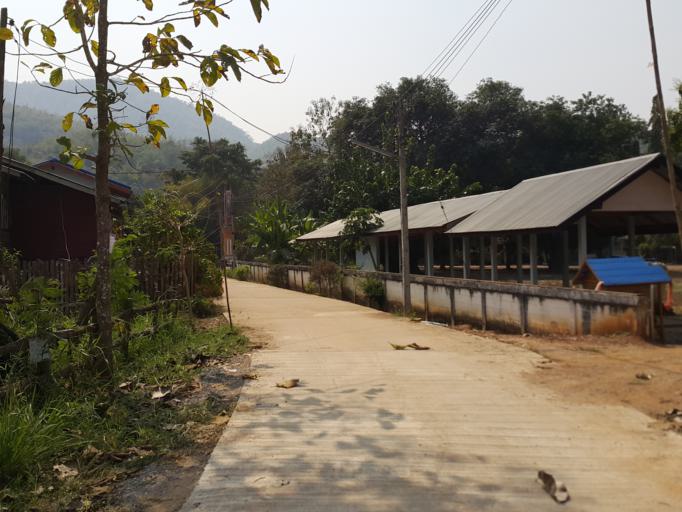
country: TH
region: Sukhothai
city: Thung Saliam
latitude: 17.3327
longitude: 99.4799
